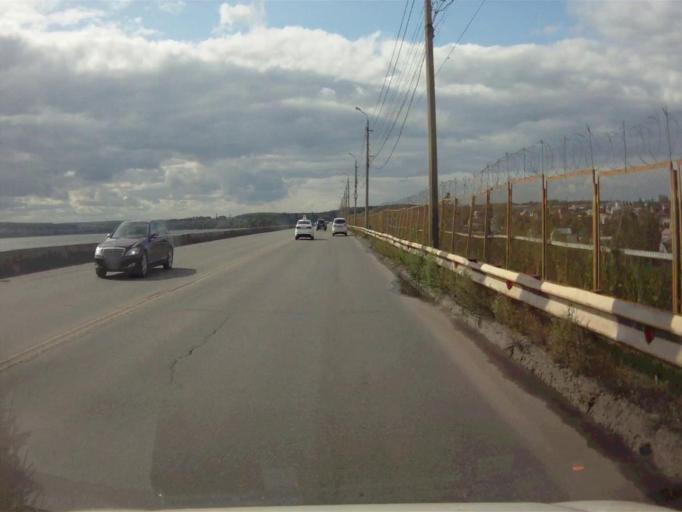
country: RU
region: Chelyabinsk
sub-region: Gorod Chelyabinsk
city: Chelyabinsk
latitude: 55.1460
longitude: 61.3181
